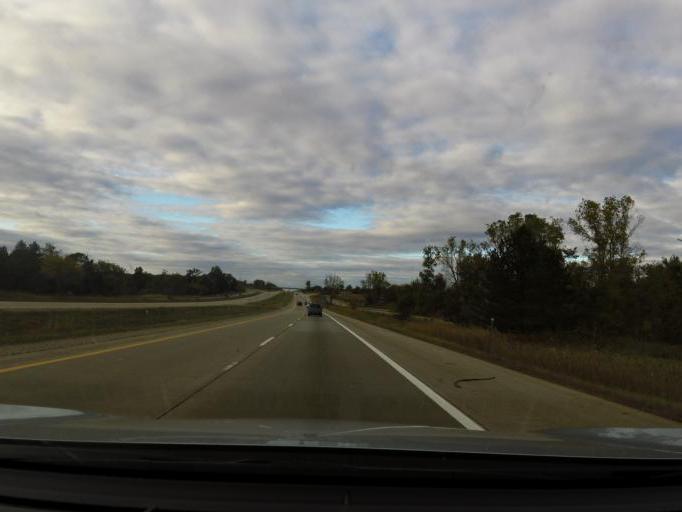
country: US
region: Michigan
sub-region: Genesee County
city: Fenton
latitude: 42.6691
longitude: -83.7595
